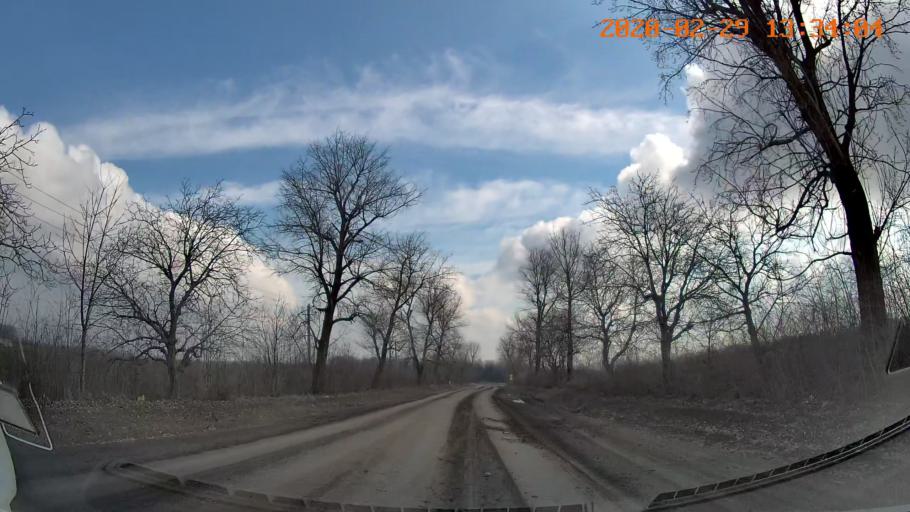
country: MD
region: Telenesti
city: Camenca
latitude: 47.8707
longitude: 28.6203
